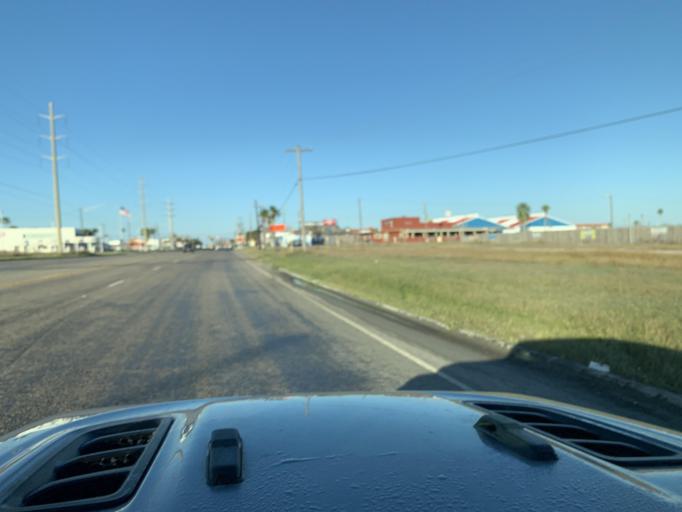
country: US
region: Texas
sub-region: Nueces County
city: Corpus Christi
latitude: 27.6180
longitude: -97.2190
